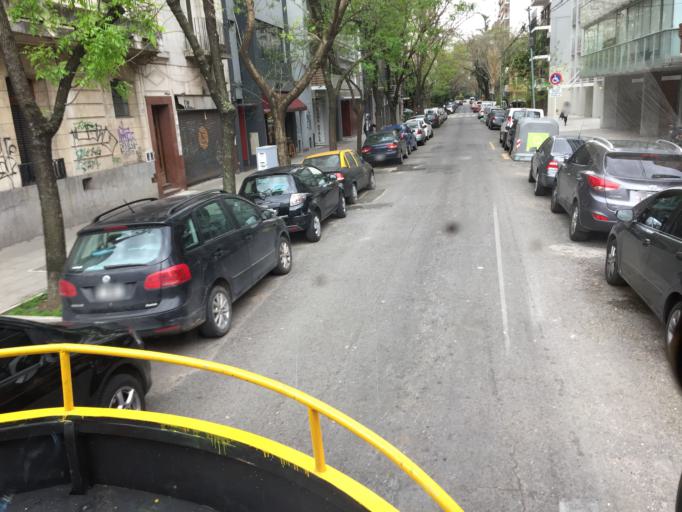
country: AR
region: Buenos Aires F.D.
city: Colegiales
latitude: -34.5711
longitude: -58.4348
